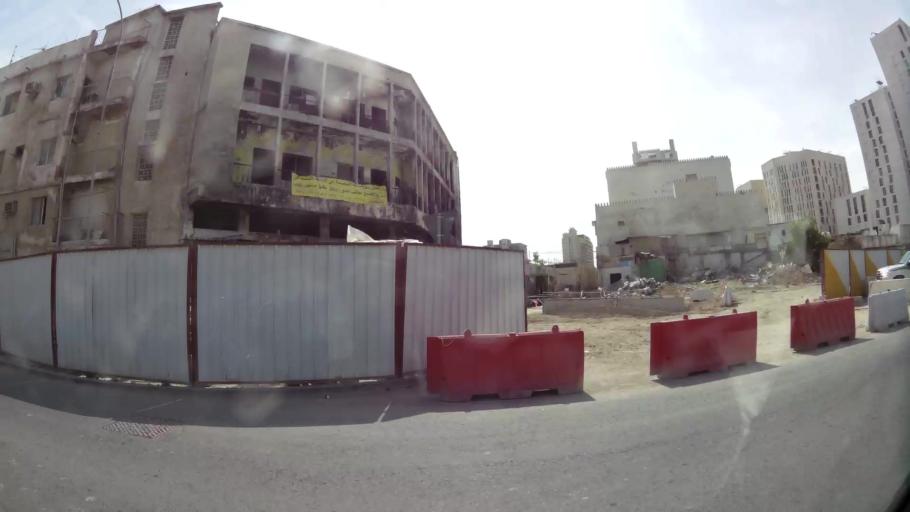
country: QA
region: Baladiyat ad Dawhah
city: Doha
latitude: 25.2845
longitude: 51.5319
